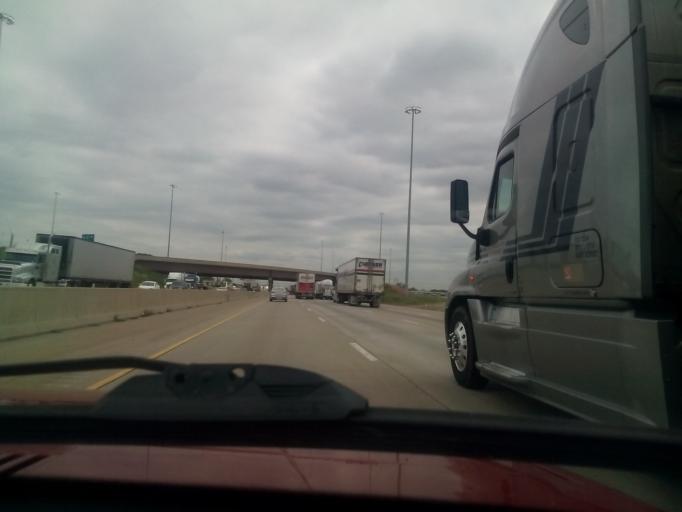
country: US
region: Illinois
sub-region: Cook County
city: Thornton
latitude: 41.5777
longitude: -87.5792
